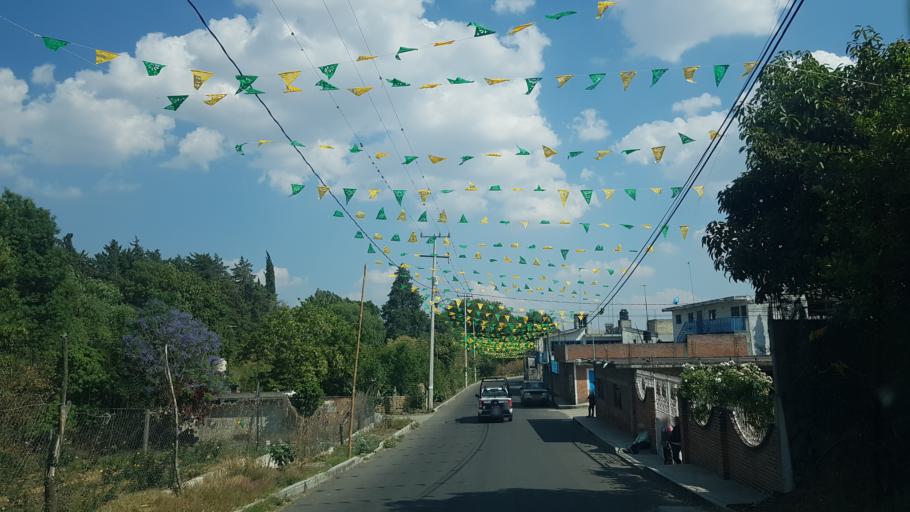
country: MX
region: Puebla
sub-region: Atlixco
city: Colonia Agricola de Ocotepec (Colonia San Jose)
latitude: 18.9239
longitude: -98.5420
